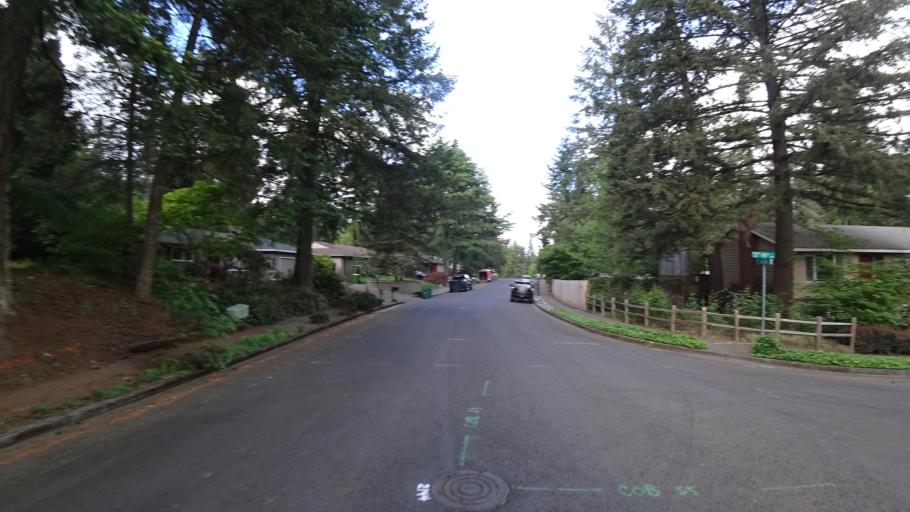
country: US
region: Oregon
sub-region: Washington County
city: Beaverton
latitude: 45.4637
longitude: -122.8210
